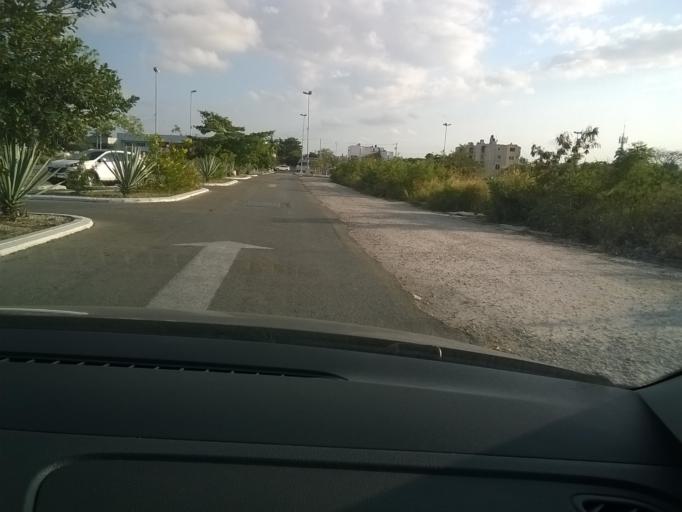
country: MX
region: Yucatan
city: Merida
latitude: 21.0294
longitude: -89.6295
